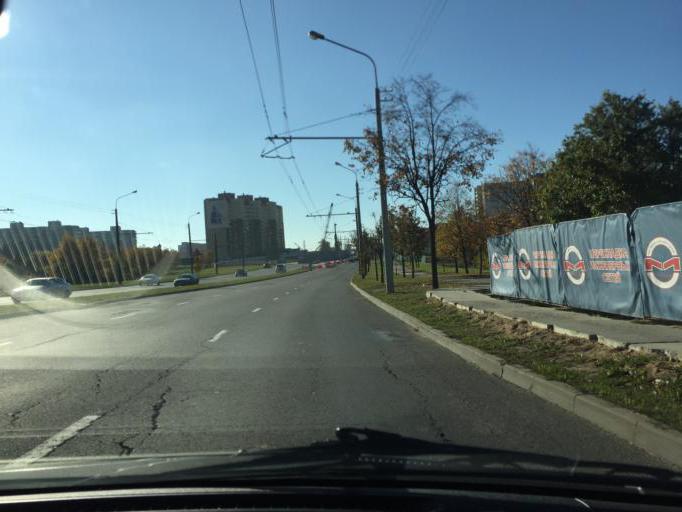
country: BY
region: Minsk
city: Syenitsa
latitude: 53.8560
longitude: 27.5387
